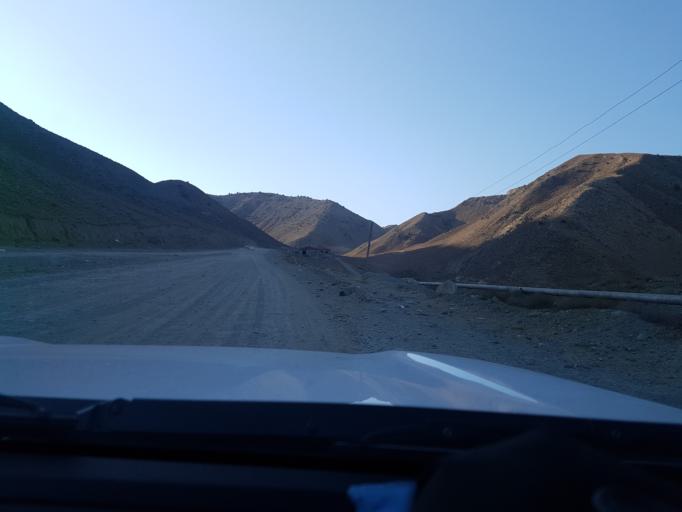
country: TM
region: Ahal
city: Baharly
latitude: 38.4525
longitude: 57.0457
